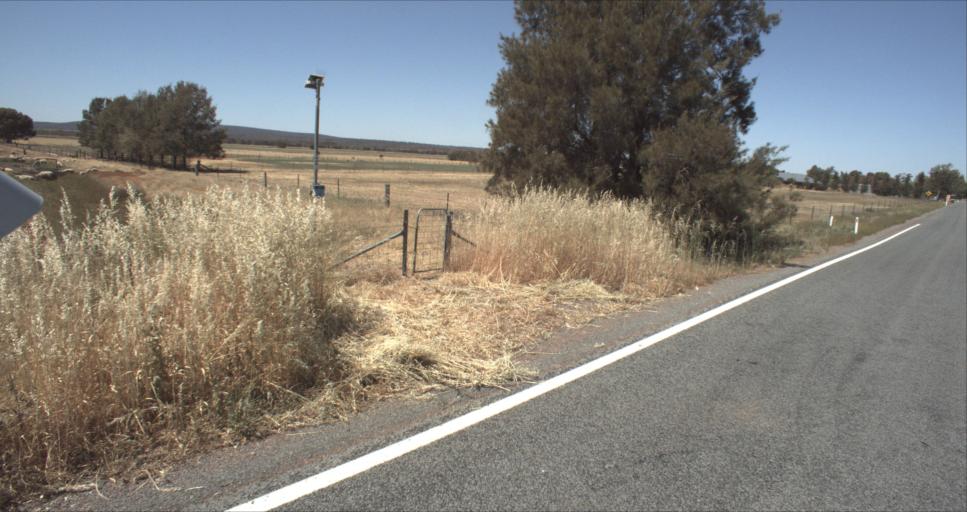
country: AU
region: New South Wales
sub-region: Leeton
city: Leeton
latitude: -34.5209
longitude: 146.4390
